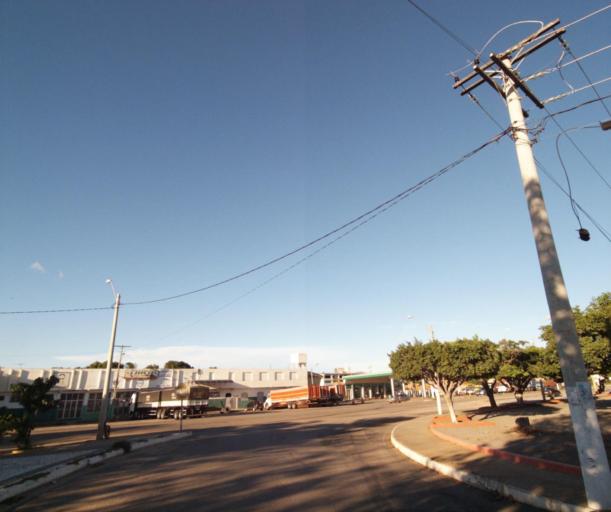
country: BR
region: Bahia
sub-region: Guanambi
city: Guanambi
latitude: -14.2110
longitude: -42.7911
